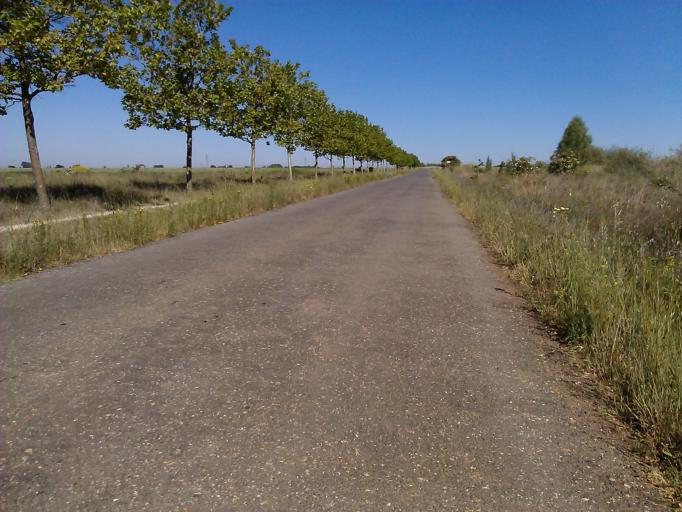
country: ES
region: Castille and Leon
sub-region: Provincia de Leon
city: Bercianos del Real Camino
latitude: 42.4016
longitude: -5.1759
